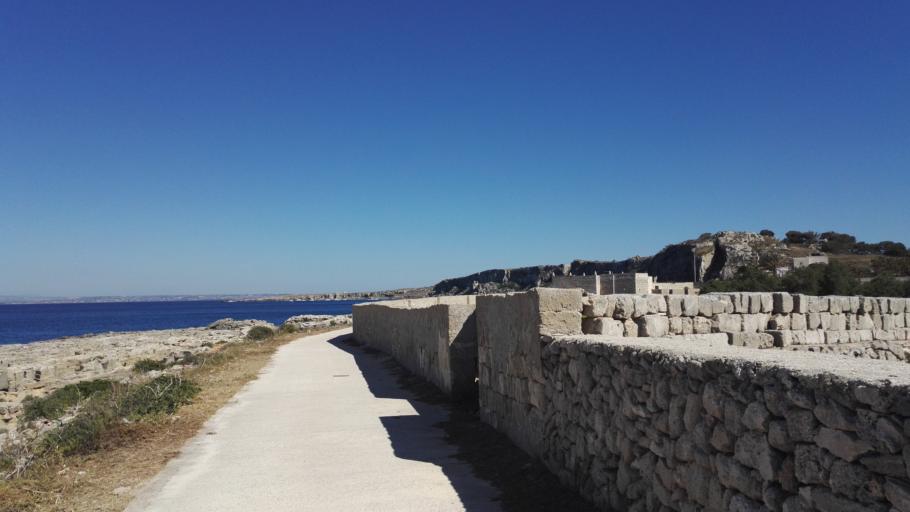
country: IT
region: Sicily
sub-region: Trapani
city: Favignana
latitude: 37.9343
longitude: 12.3484
